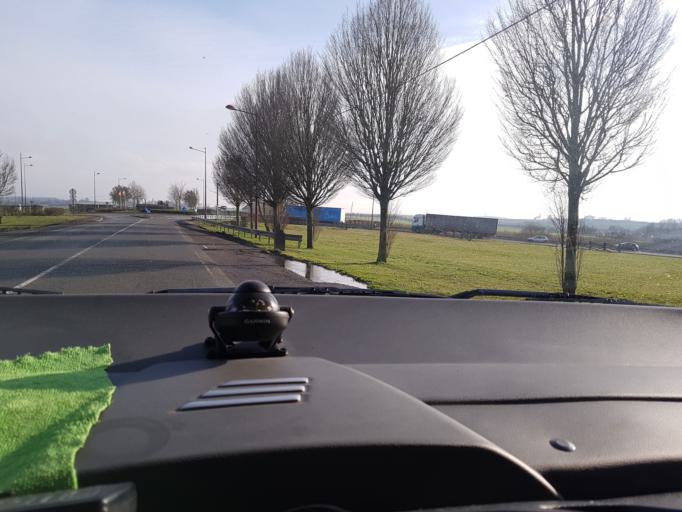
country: FR
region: Picardie
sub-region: Departement de l'Aisne
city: Hirson
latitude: 49.9058
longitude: 4.0948
